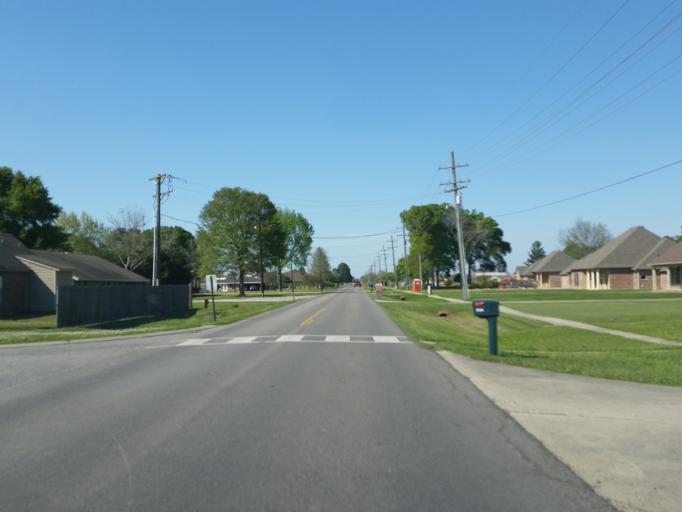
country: US
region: Louisiana
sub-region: Lafayette Parish
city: Broussard
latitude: 30.1184
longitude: -91.9652
